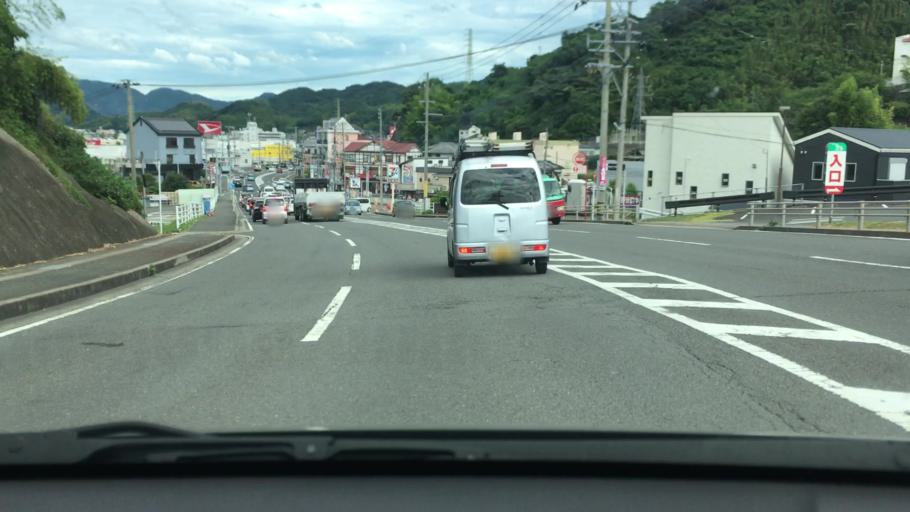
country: JP
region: Nagasaki
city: Togitsu
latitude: 32.8345
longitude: 129.8403
